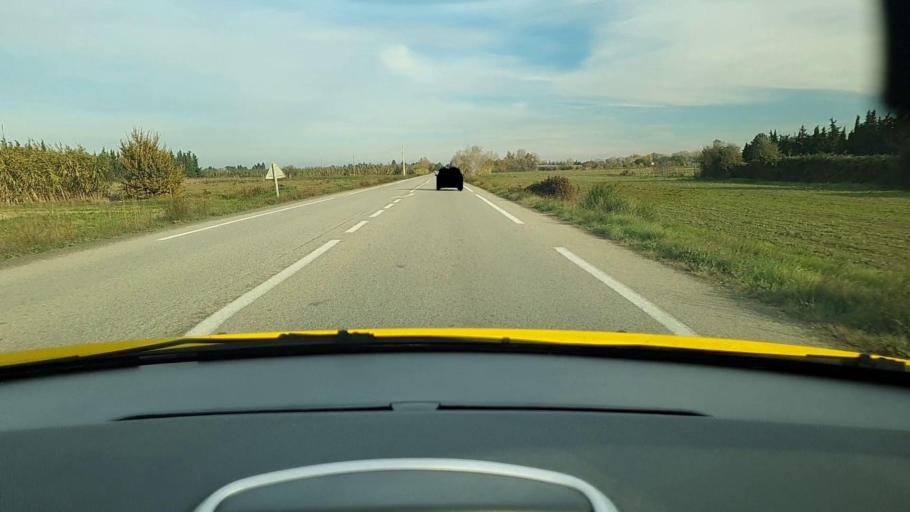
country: FR
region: Languedoc-Roussillon
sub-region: Departement du Gard
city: Fourques
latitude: 43.7001
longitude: 4.6011
